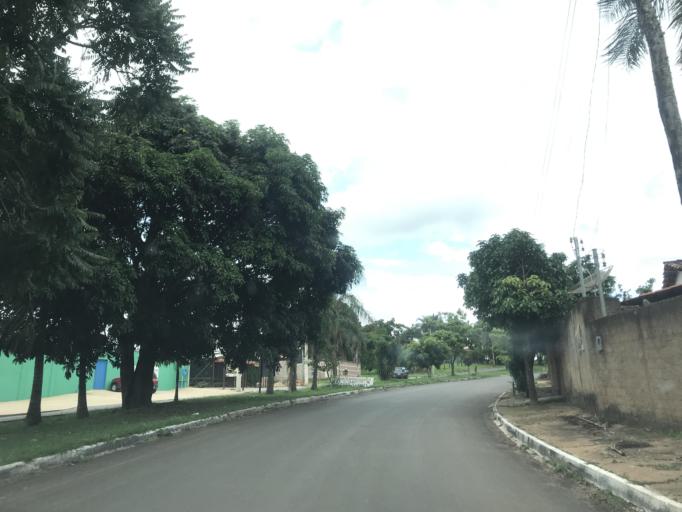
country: BR
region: Goias
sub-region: Bela Vista De Goias
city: Bela Vista de Goias
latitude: -17.0523
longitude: -48.6664
